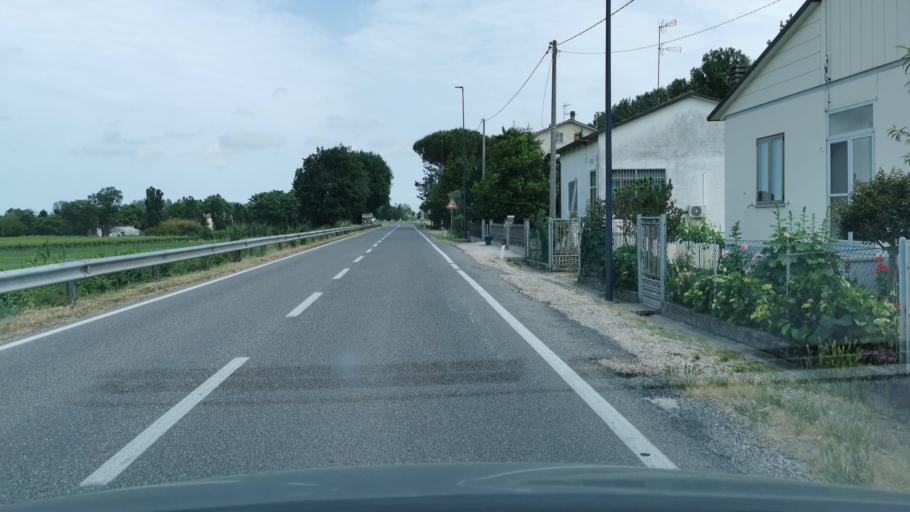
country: IT
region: Emilia-Romagna
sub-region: Provincia di Ravenna
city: Sant'Alberto
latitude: 44.5359
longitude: 12.1709
